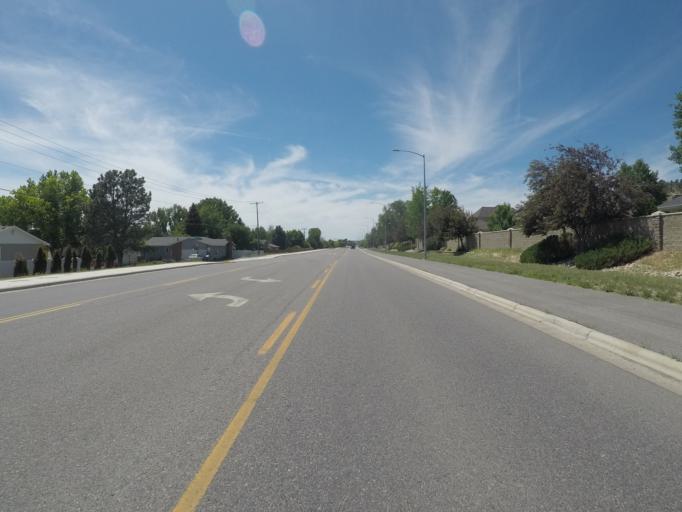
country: US
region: Montana
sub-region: Yellowstone County
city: Billings
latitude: 45.7986
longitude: -108.6049
